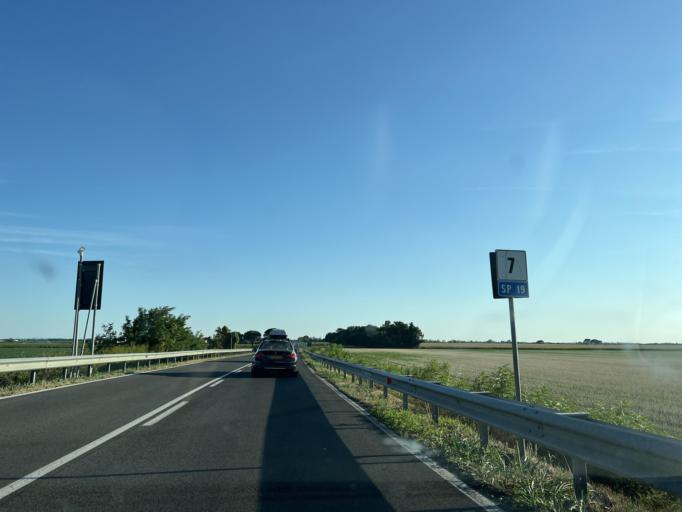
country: IT
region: Friuli Venezia Giulia
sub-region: Provincia di Gorizia
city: San Canzian d'Isonzo
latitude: 45.7655
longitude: 13.4719
